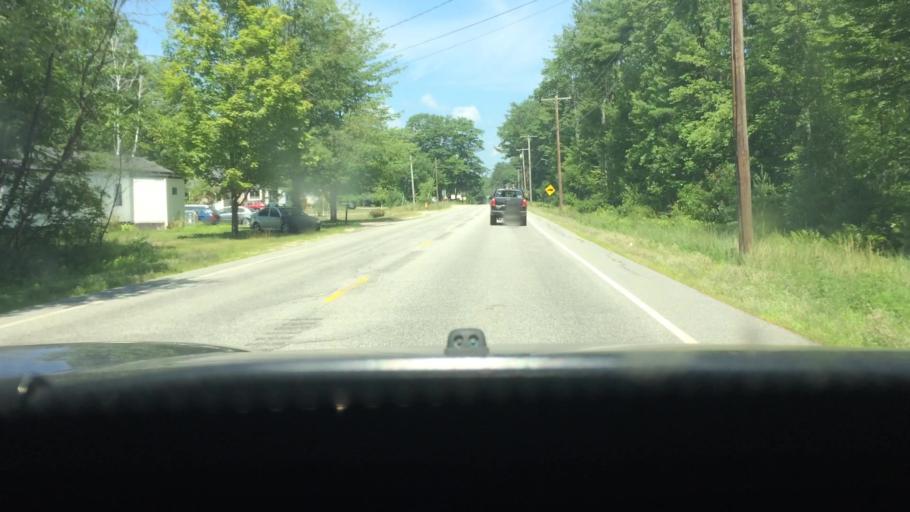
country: US
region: Maine
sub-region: Androscoggin County
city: Mechanic Falls
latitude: 44.0993
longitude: -70.3608
